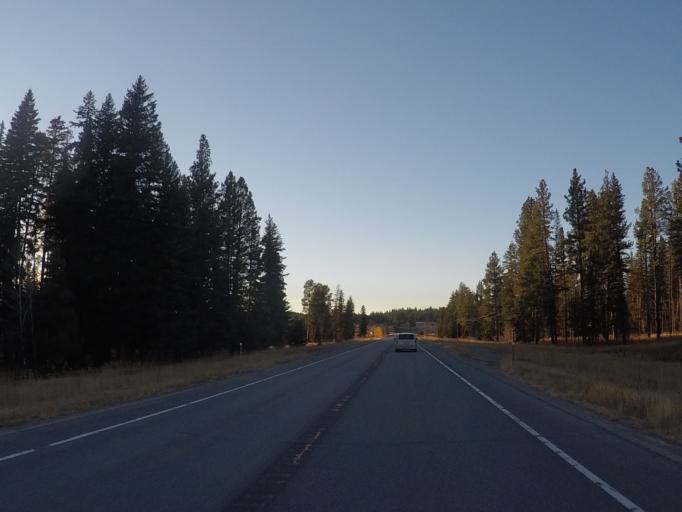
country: US
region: Montana
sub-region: Lewis and Clark County
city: Lincoln
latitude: 47.0026
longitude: -113.0408
